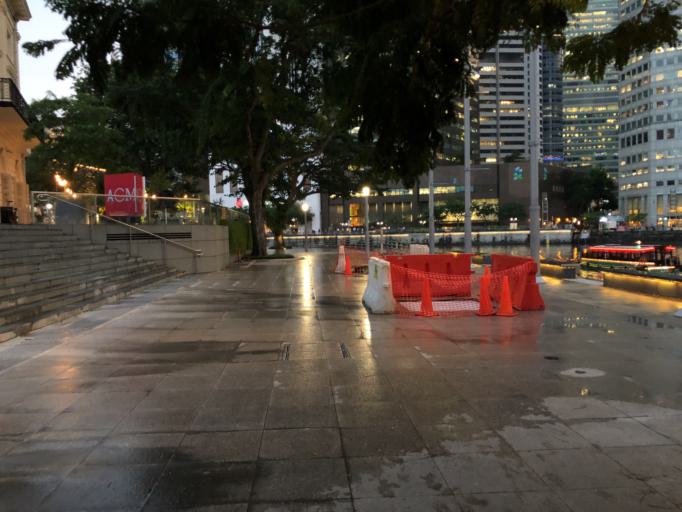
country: SG
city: Singapore
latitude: 1.2871
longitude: 103.8511
